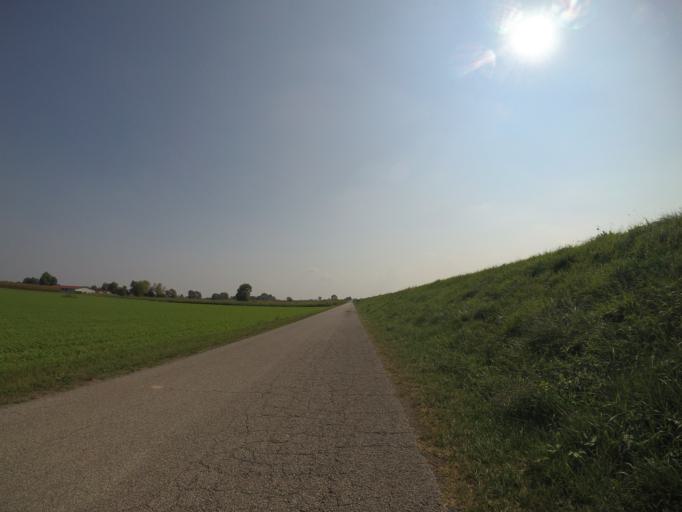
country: IT
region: Friuli Venezia Giulia
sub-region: Provincia di Udine
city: Camino al Tagliamento
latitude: 45.9370
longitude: 12.9200
